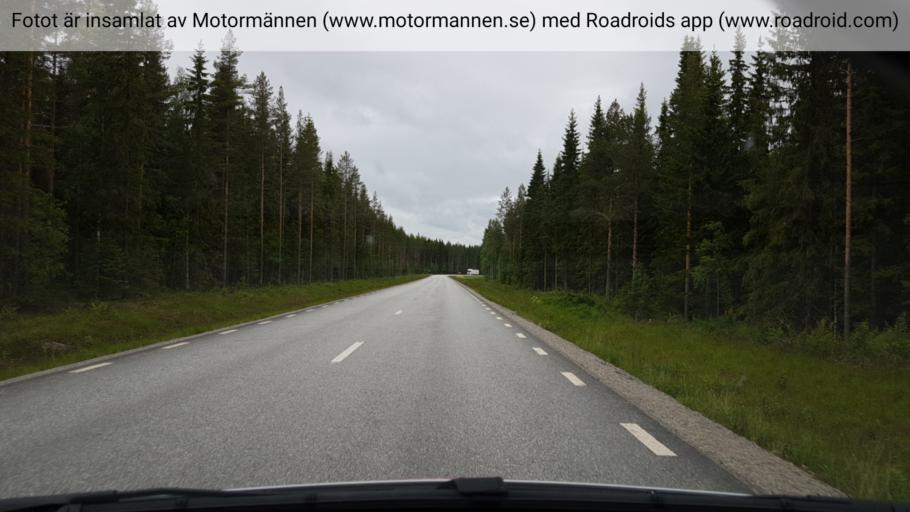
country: SE
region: Vaesterbotten
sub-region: Vindelns Kommun
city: Vindeln
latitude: 64.0894
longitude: 19.6174
